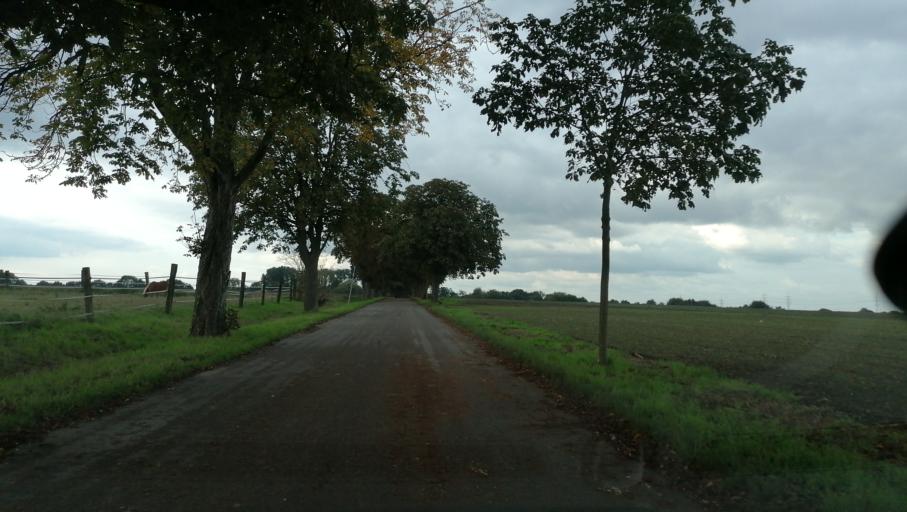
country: DE
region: North Rhine-Westphalia
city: Herten
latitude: 51.5828
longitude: 7.0931
